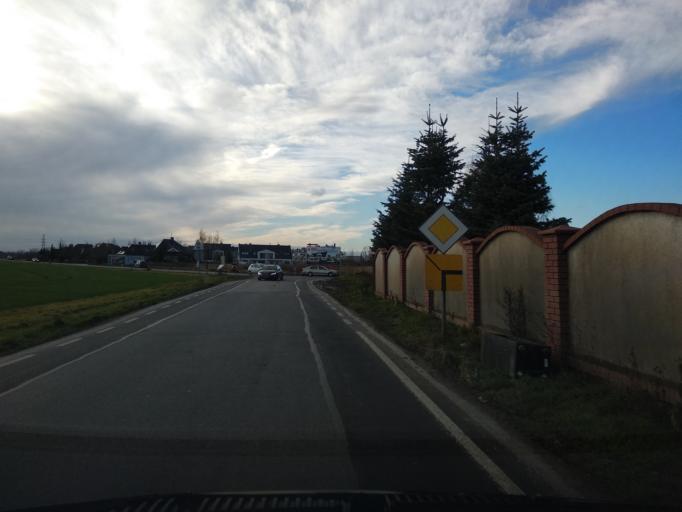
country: PL
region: Lower Silesian Voivodeship
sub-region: Powiat wroclawski
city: Zerniki Wroclawskie
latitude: 51.0426
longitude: 17.0439
